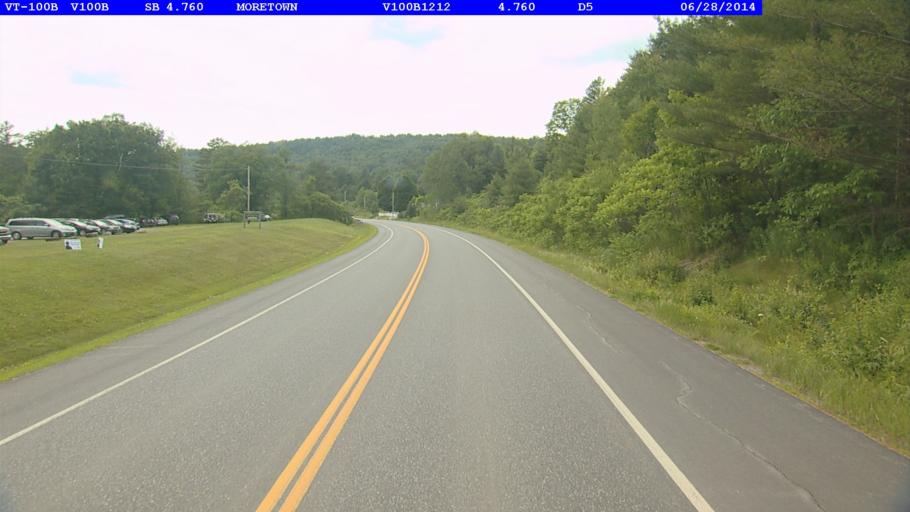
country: US
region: Vermont
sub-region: Washington County
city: Waterbury
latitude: 44.2908
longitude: -72.7238
